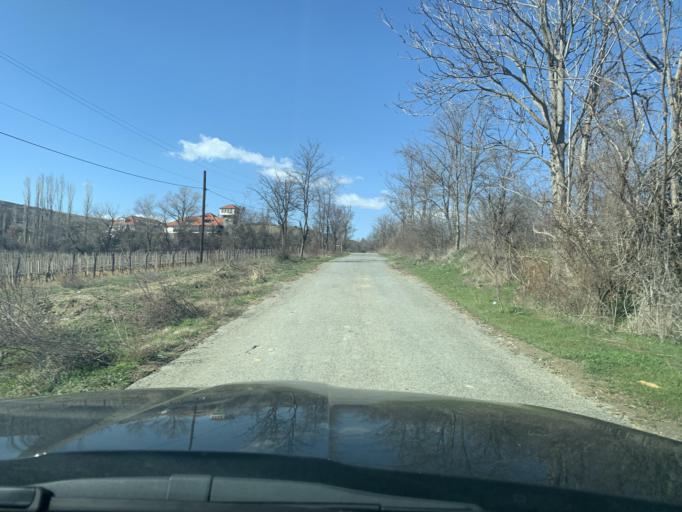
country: MK
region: Demir Kapija
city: Demir Kapija
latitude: 41.4098
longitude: 22.2291
